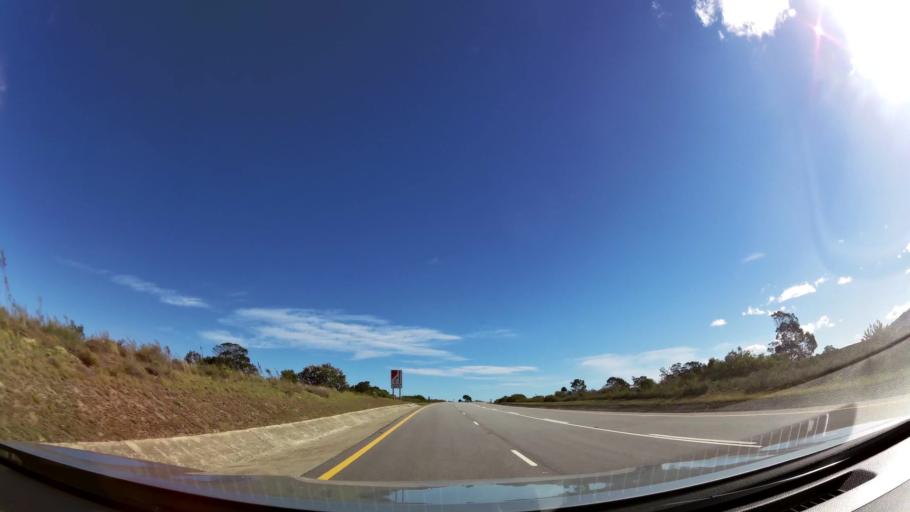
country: ZA
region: Eastern Cape
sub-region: Cacadu District Municipality
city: Kruisfontein
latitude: -34.0092
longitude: 24.6630
